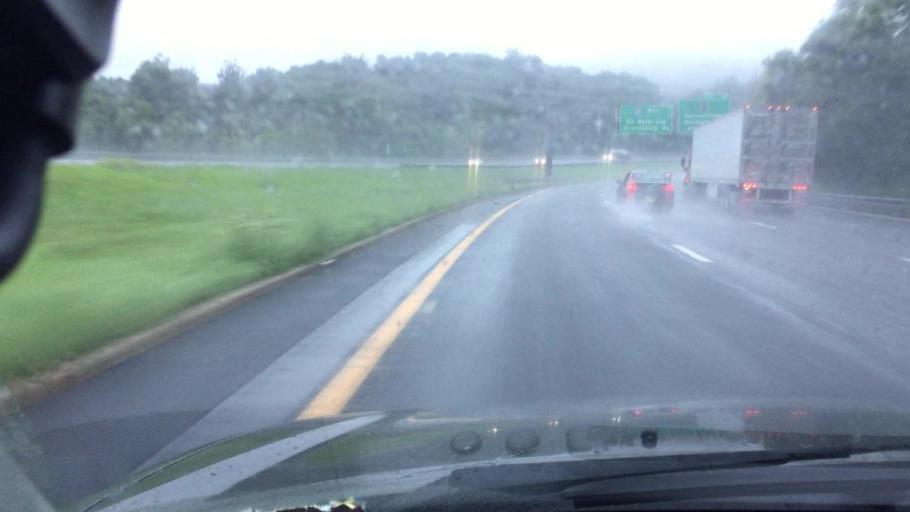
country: US
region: New Jersey
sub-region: Warren County
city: Hackettstown
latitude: 40.9176
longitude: -74.8075
